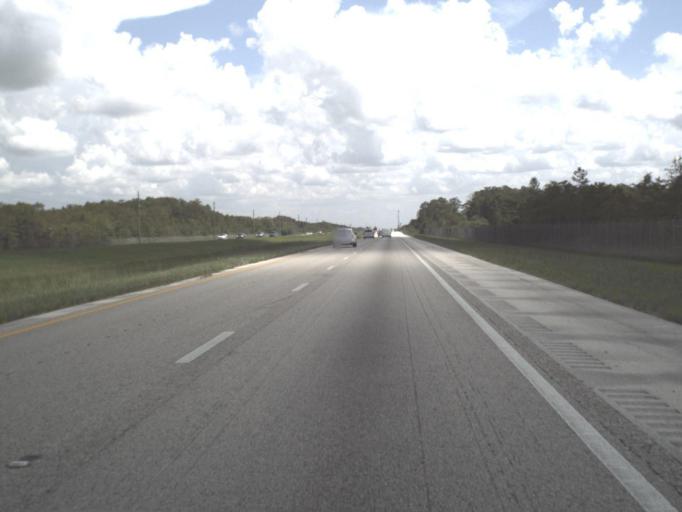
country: US
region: Florida
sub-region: Broward County
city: Weston
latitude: 26.1717
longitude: -80.9200
